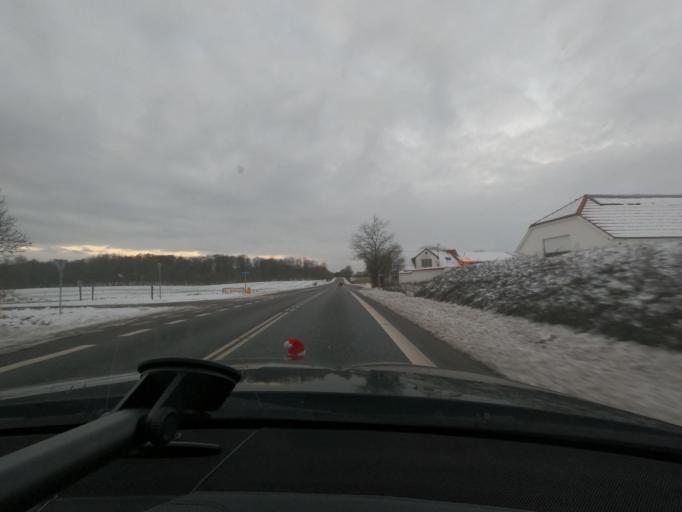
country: DE
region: Schleswig-Holstein
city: Wees
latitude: 54.8874
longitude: 9.4965
